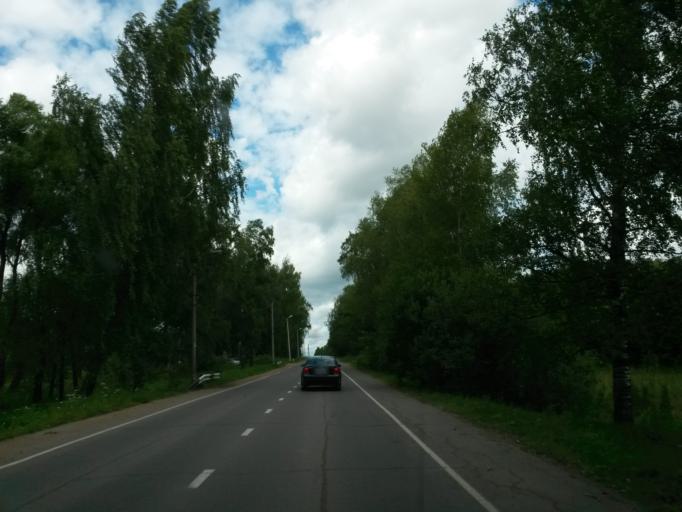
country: RU
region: Jaroslavl
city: Tutayev
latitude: 57.8952
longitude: 39.5280
